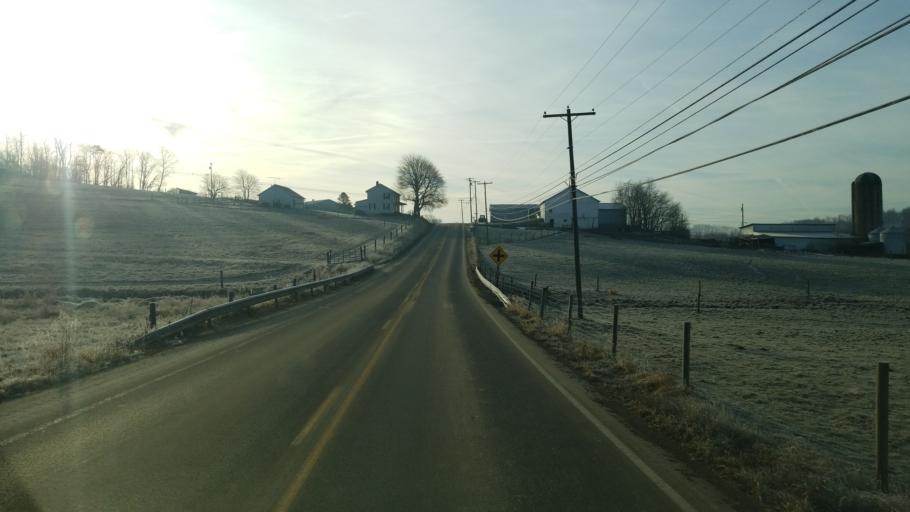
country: US
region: Pennsylvania
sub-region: Indiana County
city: Chevy Chase Heights
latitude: 40.8720
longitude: -79.2381
